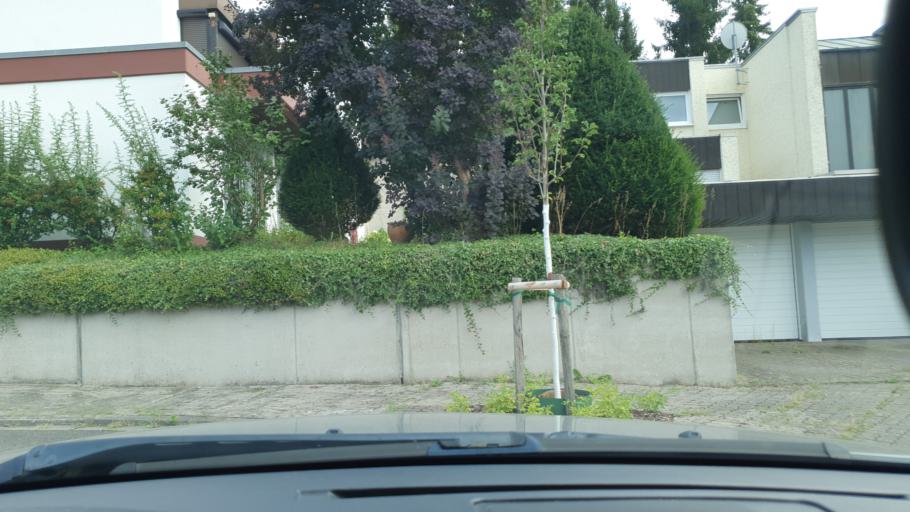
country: DE
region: Rheinland-Pfalz
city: Kaiserslautern
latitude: 49.4271
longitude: 7.7392
